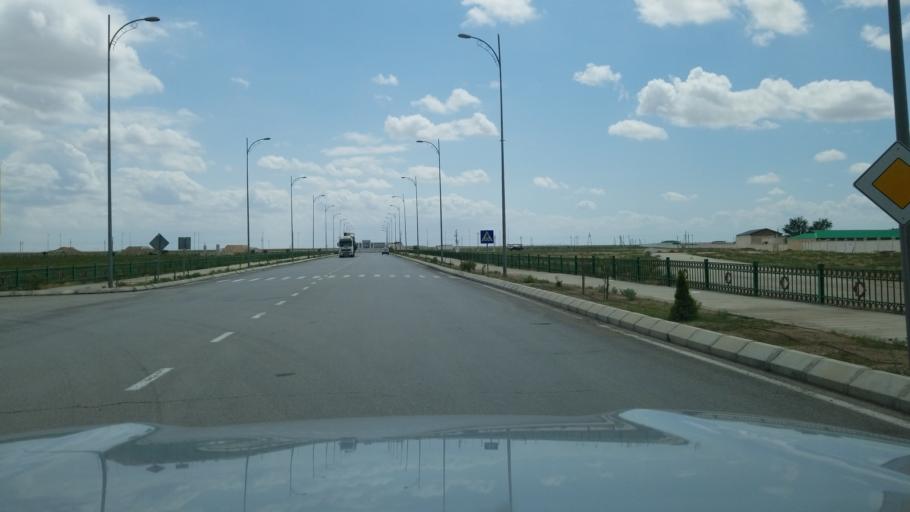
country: TM
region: Balkan
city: Balkanabat
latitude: 39.4894
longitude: 54.3766
